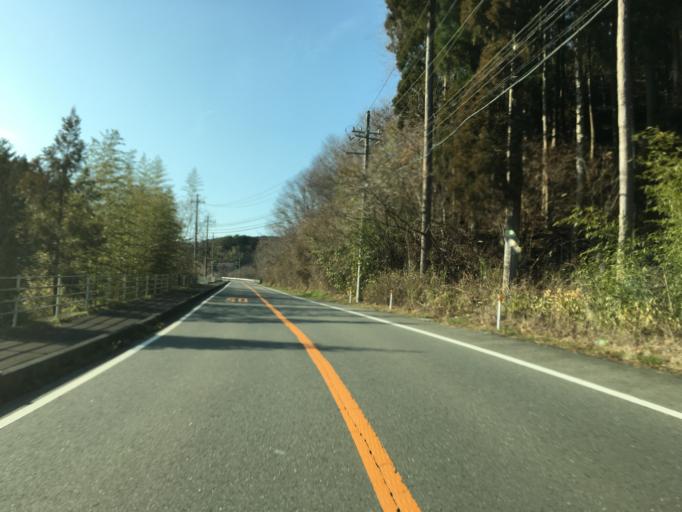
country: JP
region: Ibaraki
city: Takahagi
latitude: 36.7423
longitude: 140.6050
